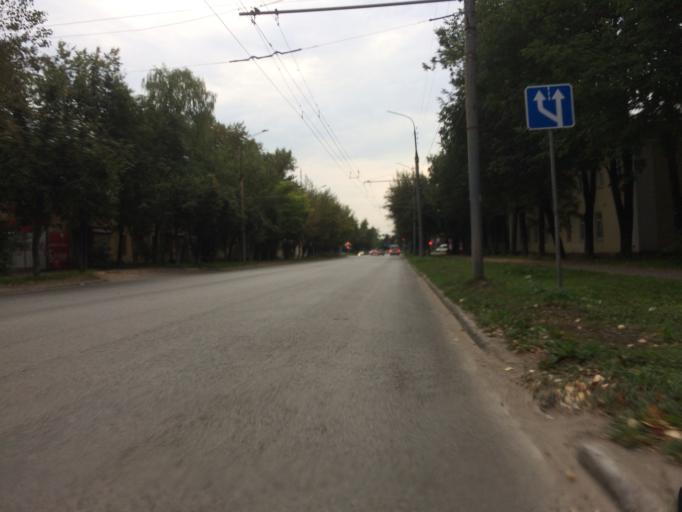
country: RU
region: Mariy-El
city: Yoshkar-Ola
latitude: 56.6369
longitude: 47.8651
